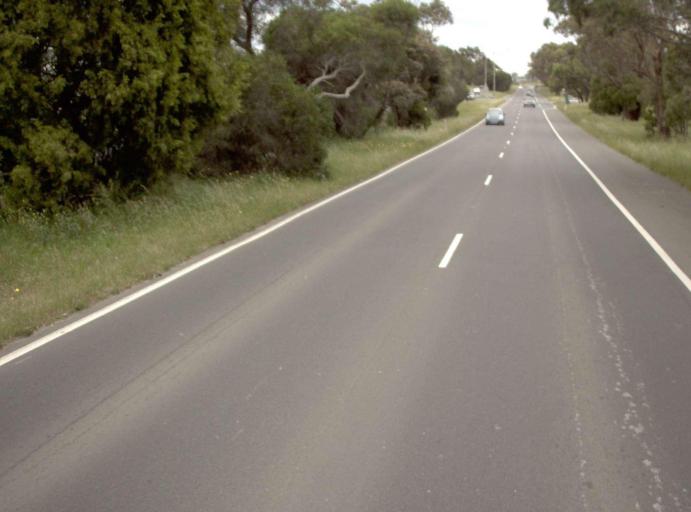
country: AU
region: Victoria
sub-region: Casey
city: Cranbourne North
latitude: -38.0704
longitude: 145.2691
